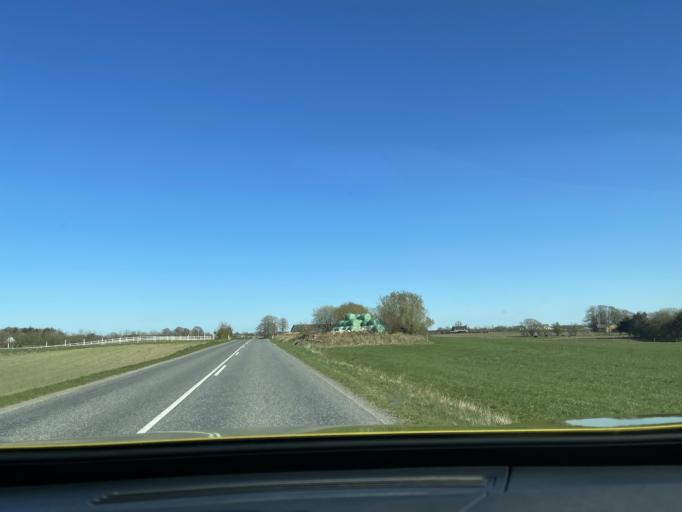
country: DK
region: Central Jutland
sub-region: Silkeborg Kommune
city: Kjellerup
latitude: 56.2593
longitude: 9.3816
